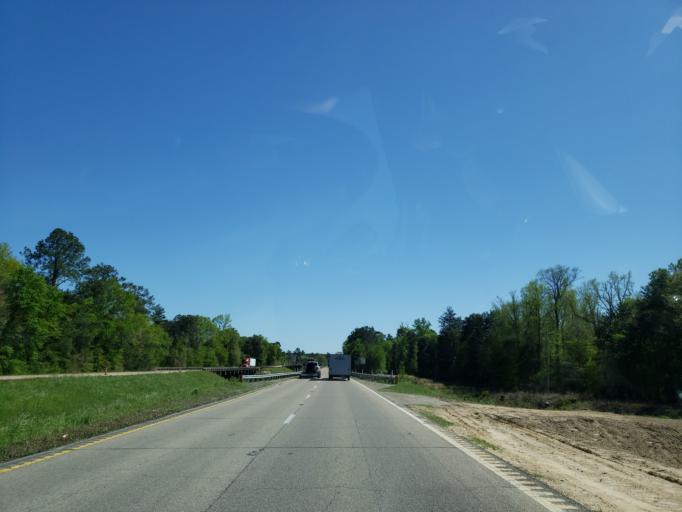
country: US
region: Mississippi
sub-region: Stone County
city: Wiggins
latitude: 31.0555
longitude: -89.2060
